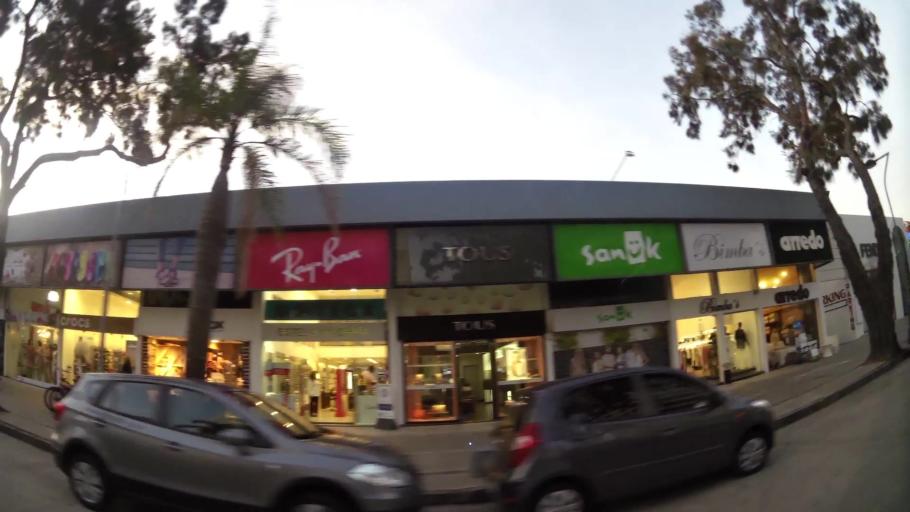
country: UY
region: Maldonado
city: Punta del Este
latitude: -34.9605
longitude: -54.9435
